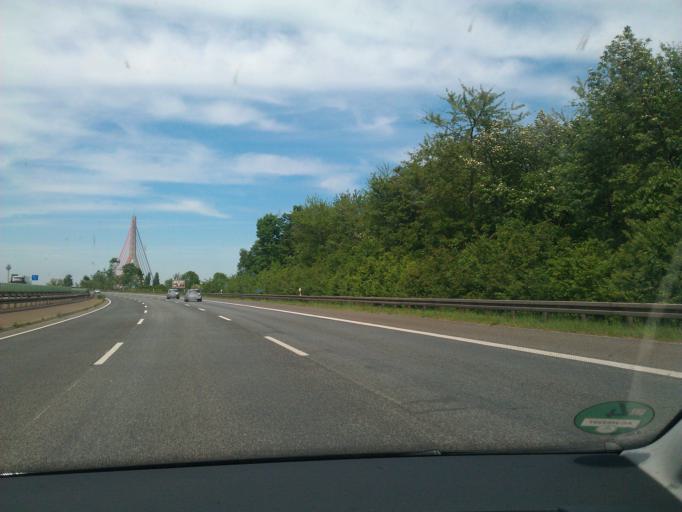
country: DE
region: North Rhine-Westphalia
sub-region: Regierungsbezirk Dusseldorf
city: Dusseldorf
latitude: 51.1718
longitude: 6.7755
